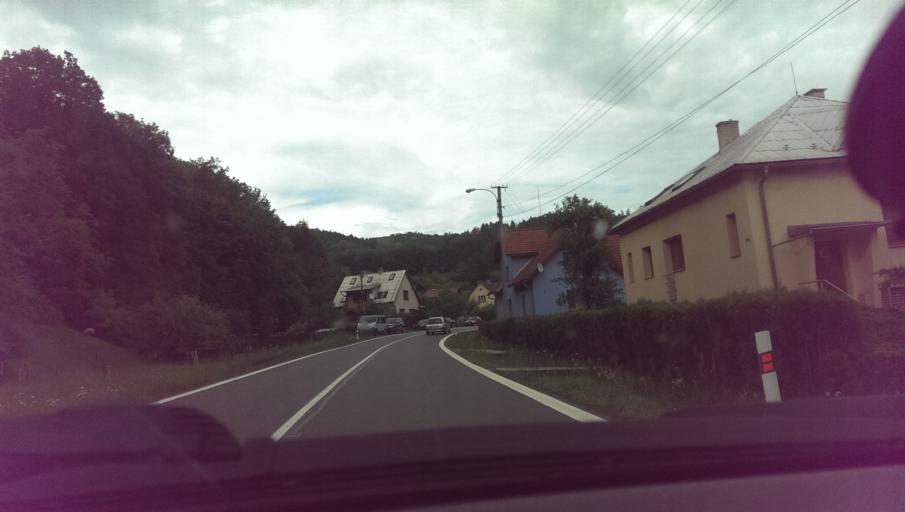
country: CZ
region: Zlin
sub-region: Okres Zlin
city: Vizovice
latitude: 49.2249
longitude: 17.9064
